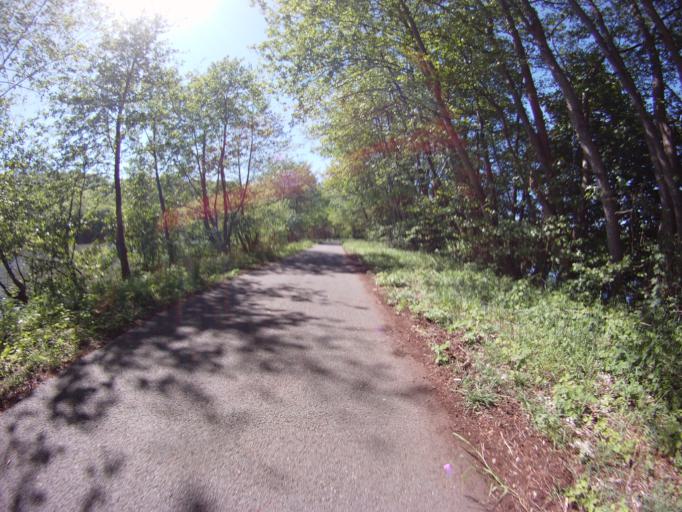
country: FR
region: Lorraine
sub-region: Departement de Meurthe-et-Moselle
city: Velaine-en-Haye
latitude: 48.6550
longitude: 6.0014
